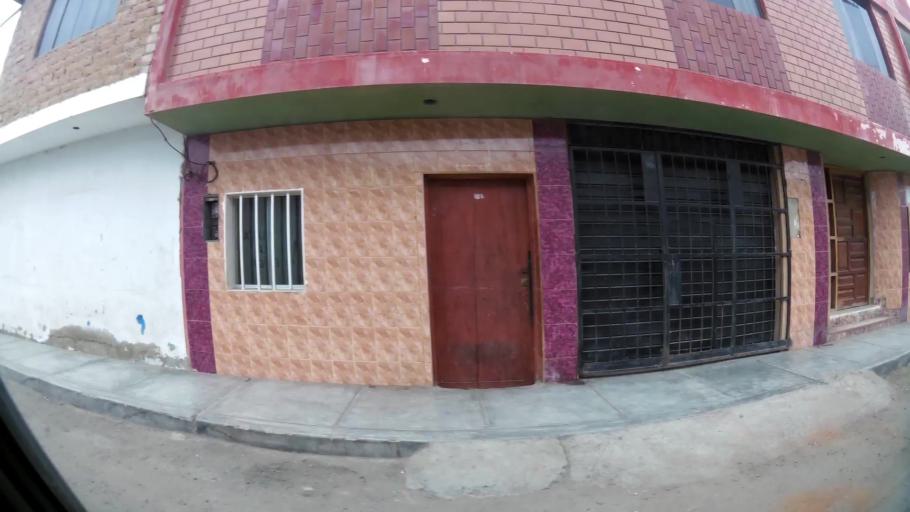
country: PE
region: La Libertad
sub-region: Provincia de Trujillo
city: La Esperanza
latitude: -8.0991
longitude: -79.0625
